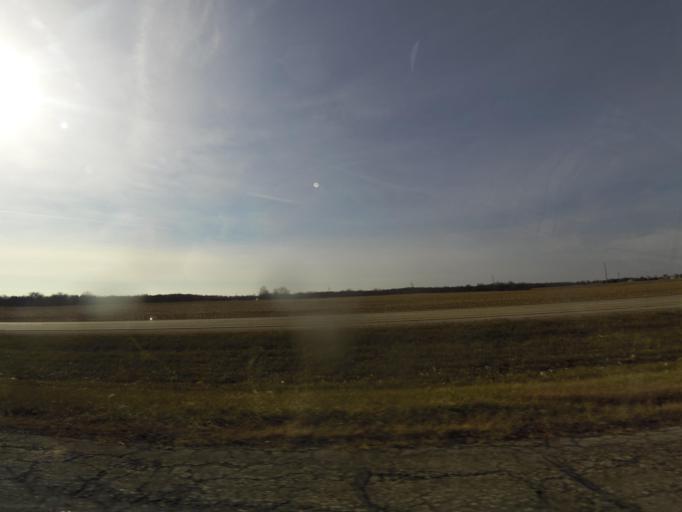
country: US
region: Illinois
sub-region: De Witt County
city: Clinton
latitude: 40.1377
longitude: -88.9763
